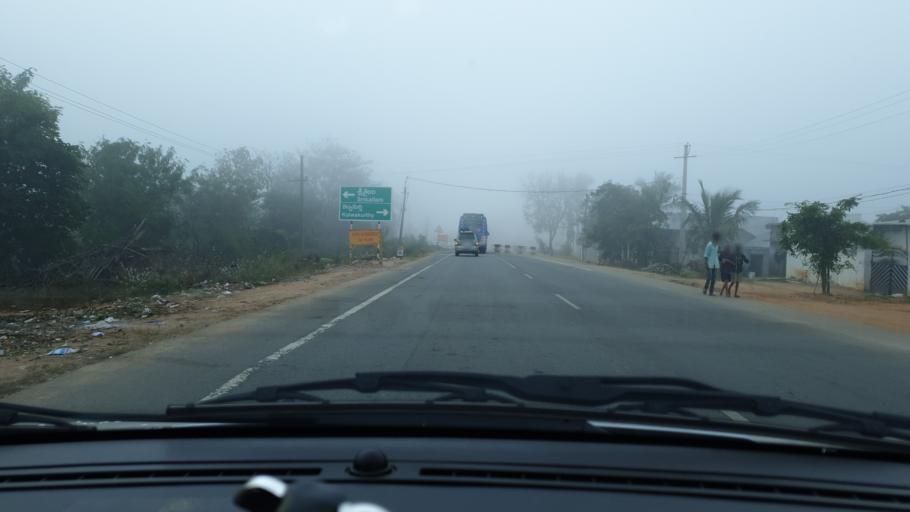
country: IN
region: Telangana
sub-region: Mahbubnagar
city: Nagar Karnul
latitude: 16.6630
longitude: 78.5308
